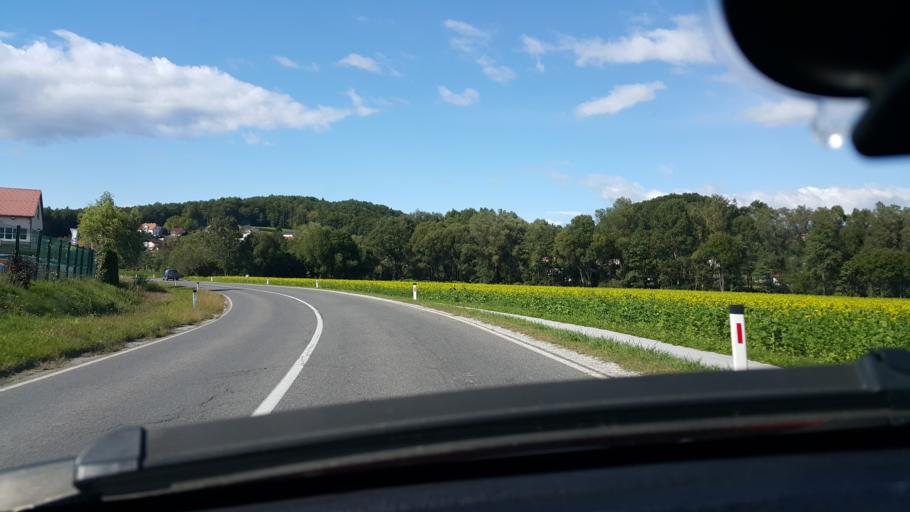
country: SI
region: Pesnica
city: Pesnica pri Mariboru
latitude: 46.6160
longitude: 15.6434
